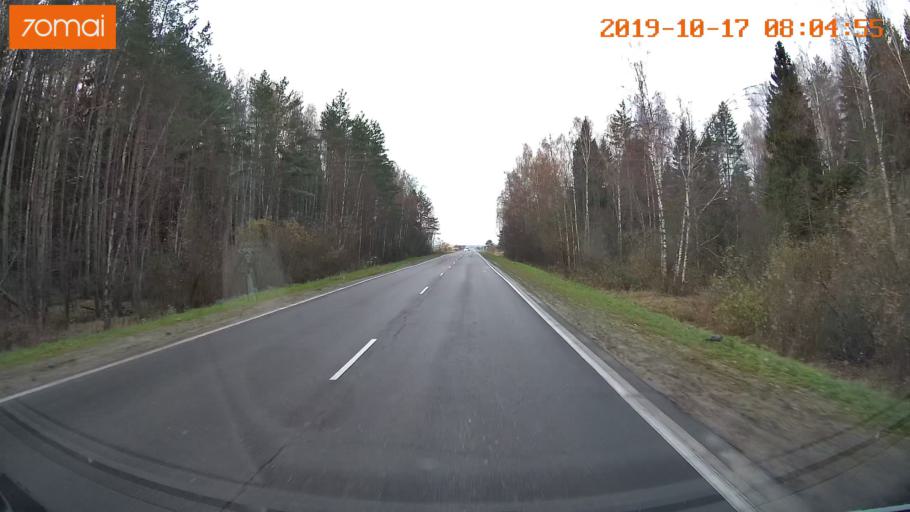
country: RU
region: Vladimir
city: Belaya Rechka
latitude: 56.3402
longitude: 39.4258
